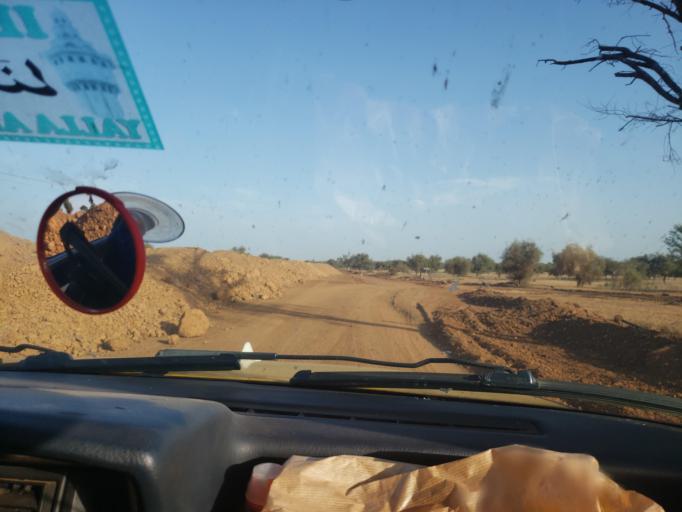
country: SN
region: Louga
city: Dara
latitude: 15.4151
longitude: -15.7093
